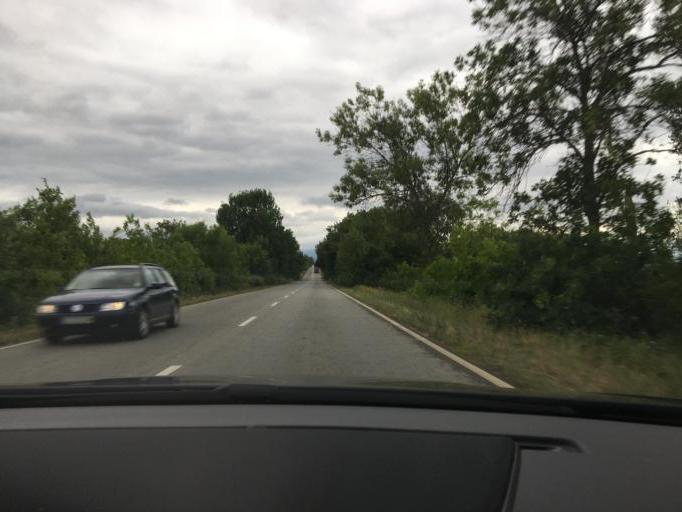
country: BG
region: Kyustendil
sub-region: Obshtina Kyustendil
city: Kyustendil
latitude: 42.2689
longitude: 22.7972
